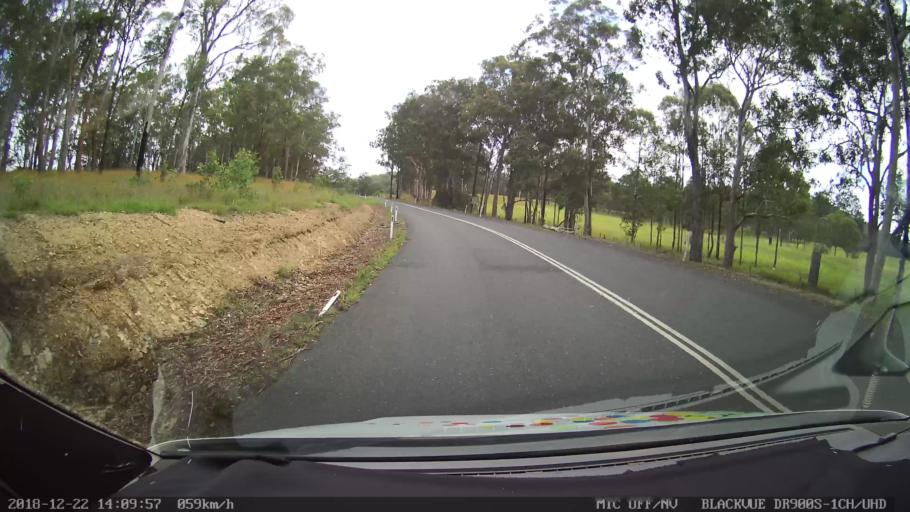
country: AU
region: New South Wales
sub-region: Clarence Valley
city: Coutts Crossing
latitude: -29.9894
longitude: 152.7124
